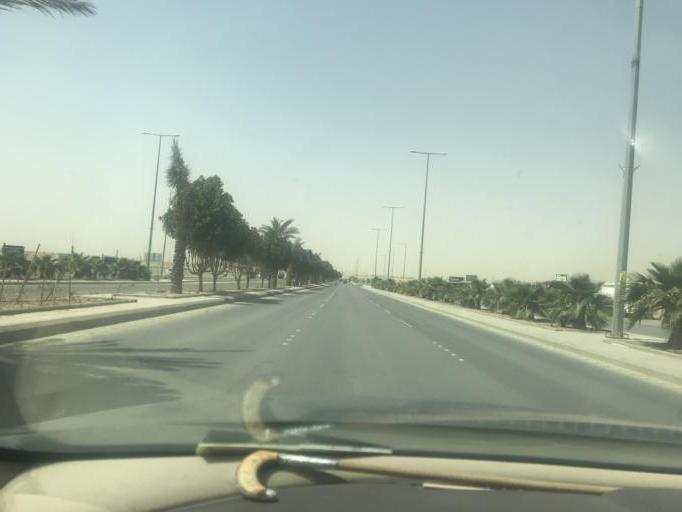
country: SA
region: Ar Riyad
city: Riyadh
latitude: 24.8027
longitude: 46.5828
